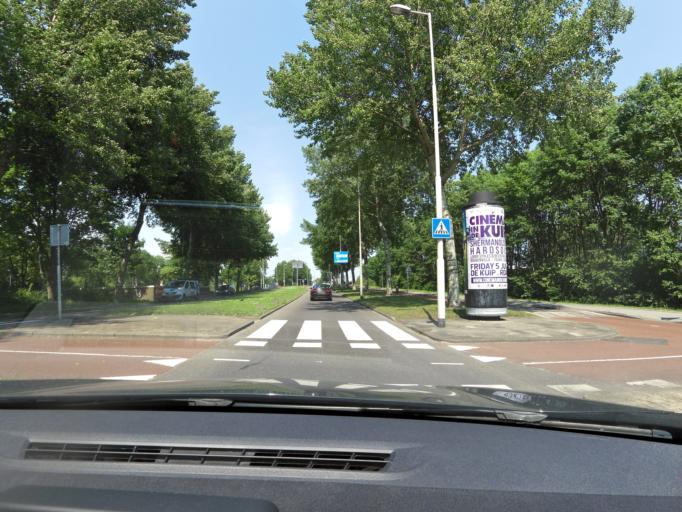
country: NL
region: South Holland
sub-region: Gemeente Rotterdam
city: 's-Gravenland
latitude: 51.9205
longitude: 4.5306
